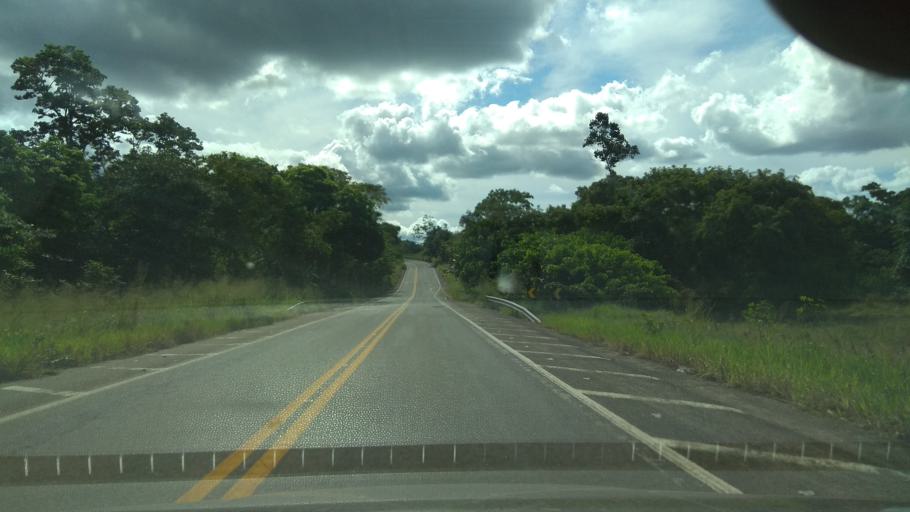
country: BR
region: Bahia
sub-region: Ubaitaba
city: Ubaitaba
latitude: -14.2492
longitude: -39.3576
